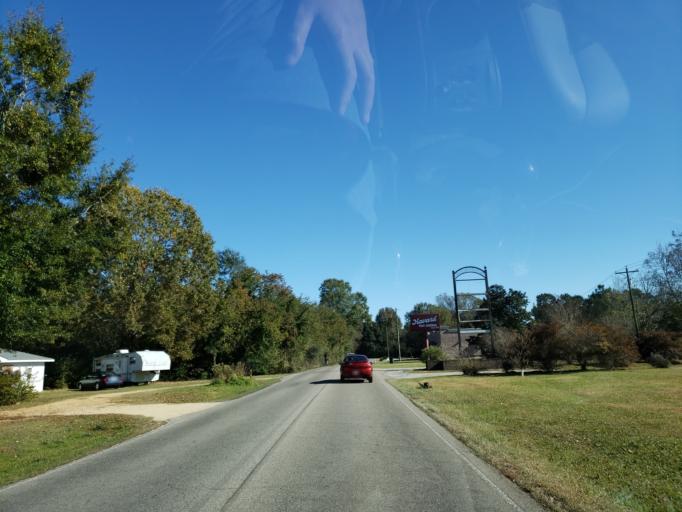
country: US
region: Mississippi
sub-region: Lamar County
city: West Hattiesburg
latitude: 31.3073
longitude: -89.3896
